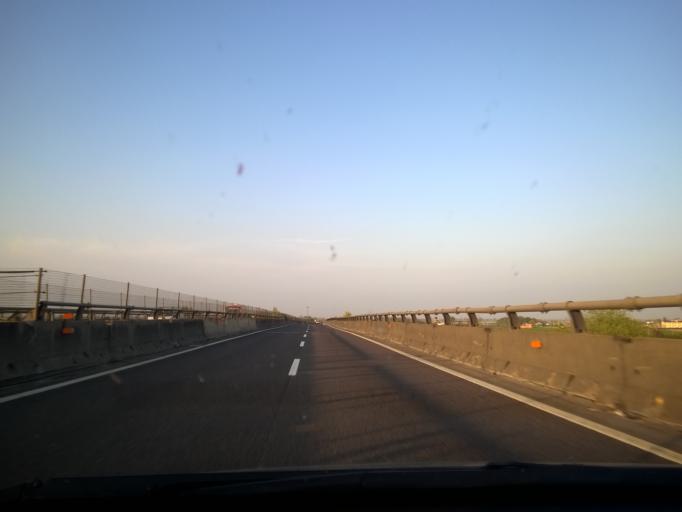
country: IT
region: Veneto
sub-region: Provincia di Rovigo
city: Occhiobello
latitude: 44.9176
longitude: 11.5819
